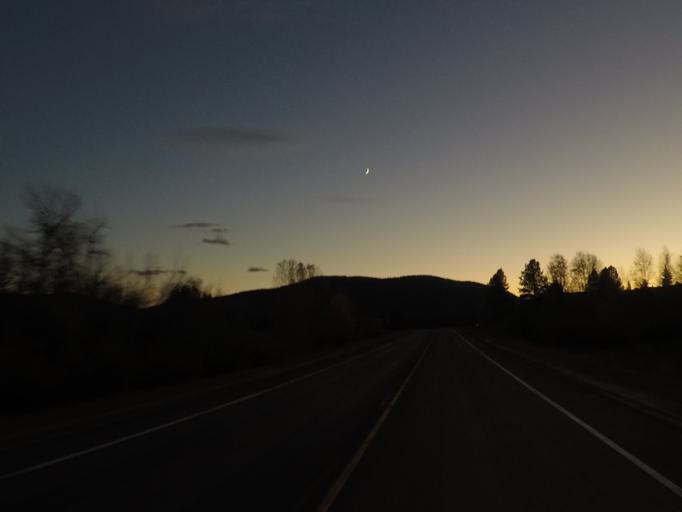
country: US
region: Montana
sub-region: Missoula County
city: Seeley Lake
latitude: 47.0369
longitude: -113.2284
